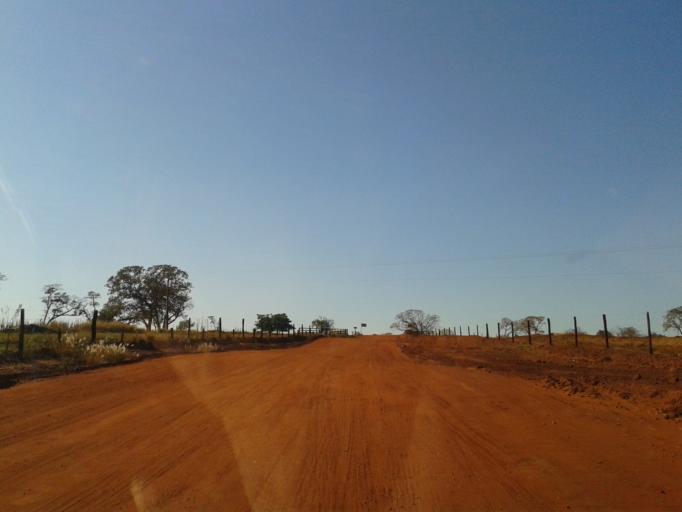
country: BR
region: Minas Gerais
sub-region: Ituiutaba
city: Ituiutaba
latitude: -18.9759
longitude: -49.4121
